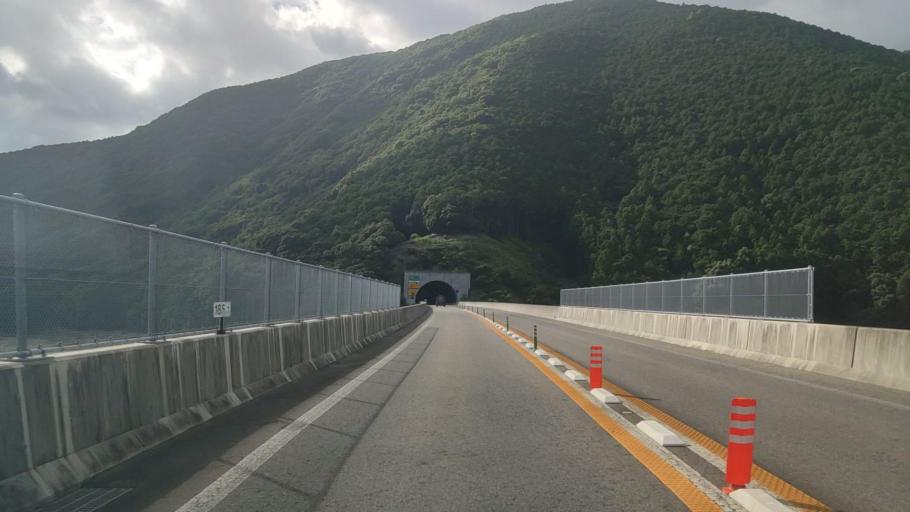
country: JP
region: Wakayama
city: Tanabe
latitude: 33.5605
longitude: 135.5052
